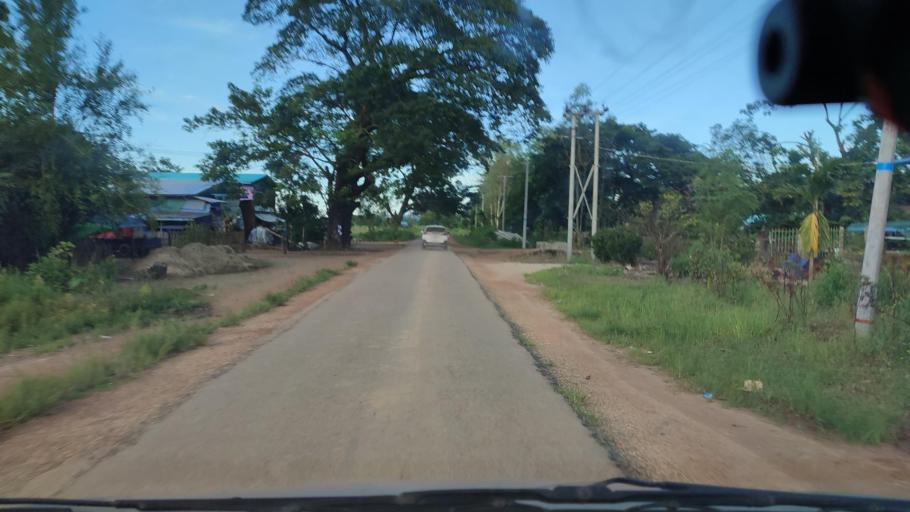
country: MM
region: Bago
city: Tharyarwady
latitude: 17.7109
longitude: 95.8131
